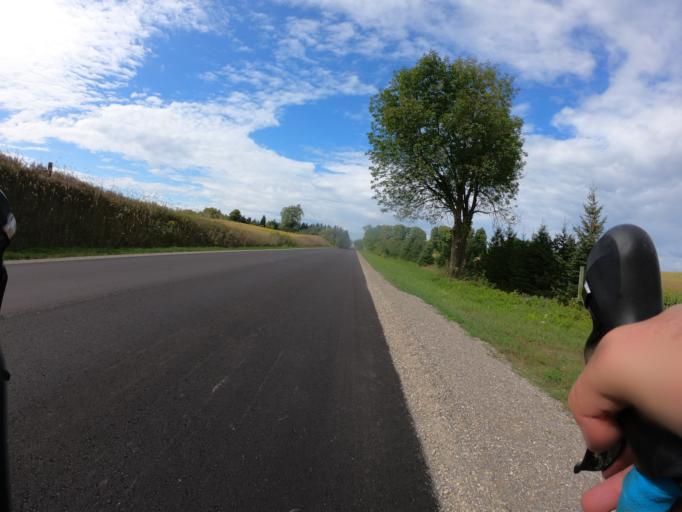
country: CA
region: Ontario
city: Kitchener
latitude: 43.3815
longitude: -80.6229
